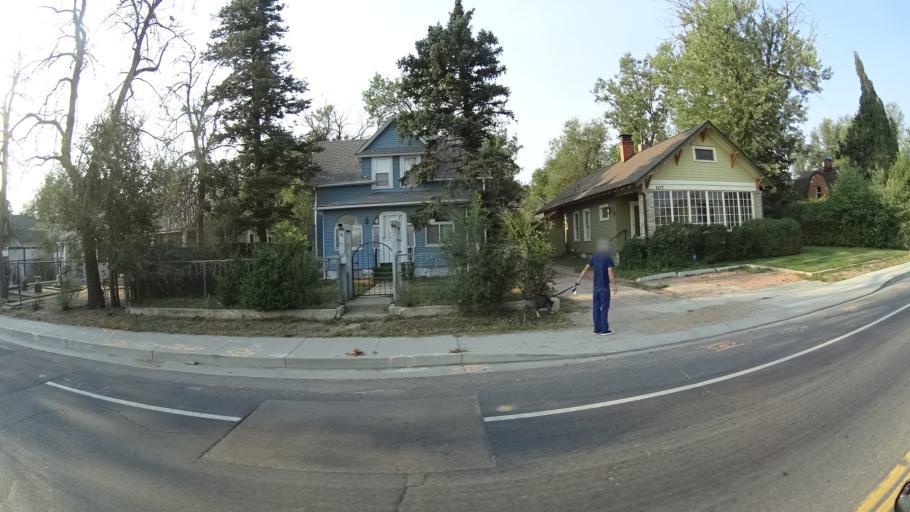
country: US
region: Colorado
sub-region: El Paso County
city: Colorado Springs
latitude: 38.8067
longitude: -104.8248
